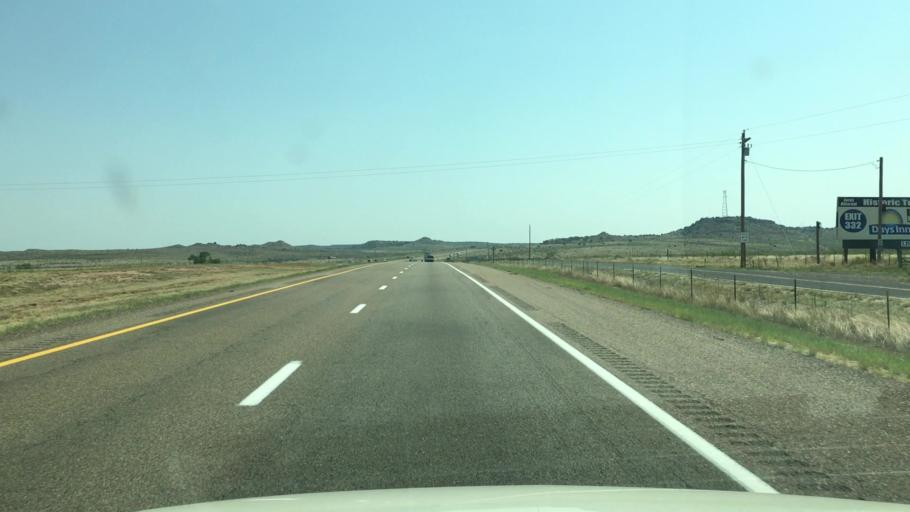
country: US
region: New Mexico
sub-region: Quay County
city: Tucumcari
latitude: 35.1217
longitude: -103.9668
